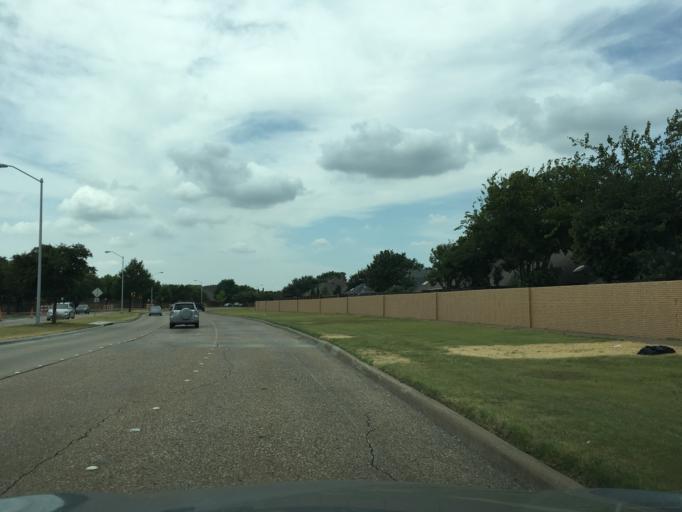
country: US
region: Texas
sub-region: Collin County
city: Plano
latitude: 33.0572
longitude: -96.7563
